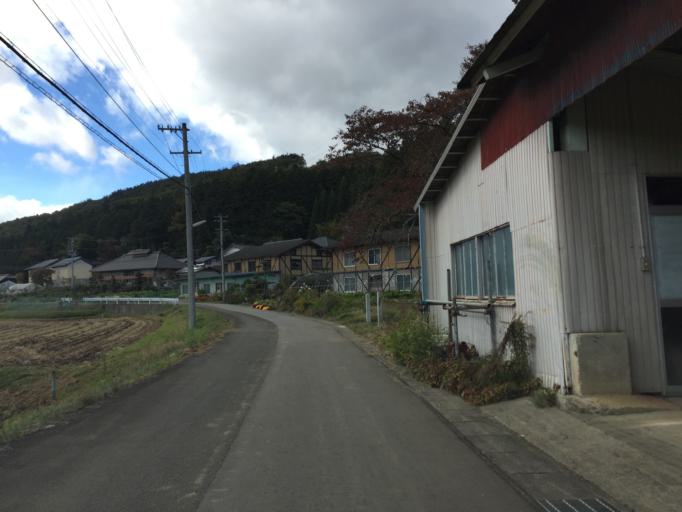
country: JP
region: Fukushima
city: Nihommatsu
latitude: 37.6735
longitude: 140.4107
